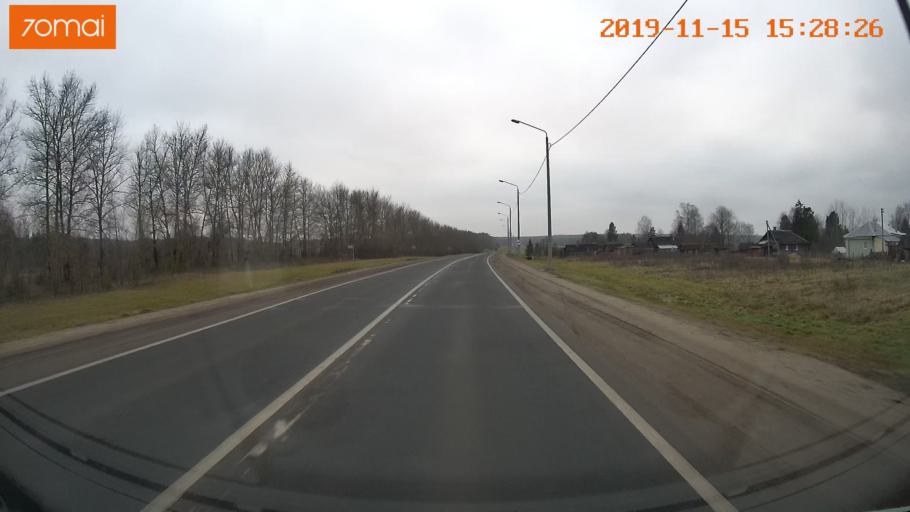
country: RU
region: Jaroslavl
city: Danilov
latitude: 58.1322
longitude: 40.1349
